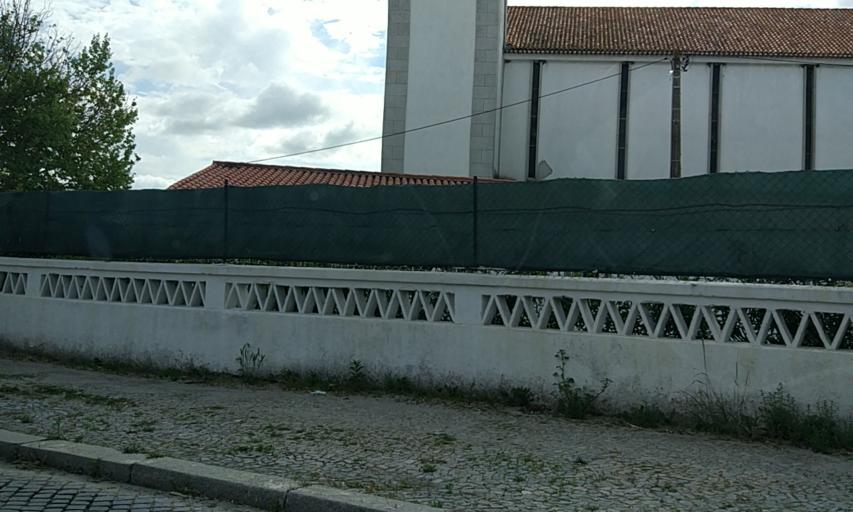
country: PT
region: Evora
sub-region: Evora
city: Evora
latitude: 38.5695
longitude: -7.9143
